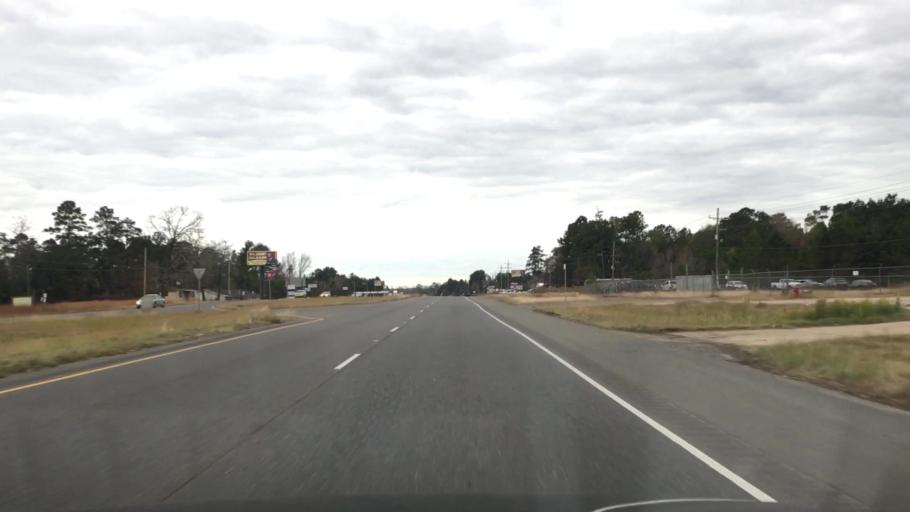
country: US
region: Louisiana
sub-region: Vernon Parish
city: New Llano
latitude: 31.0795
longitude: -93.2728
